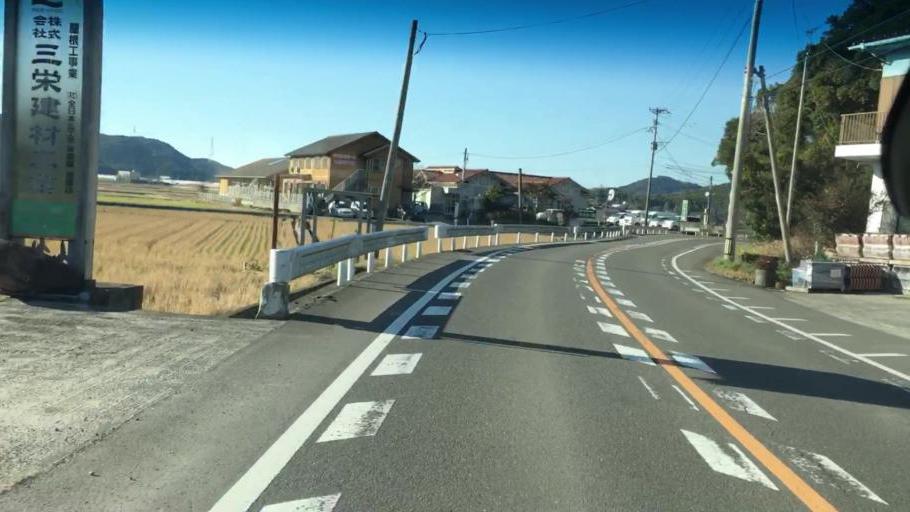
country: JP
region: Kagoshima
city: Satsumasendai
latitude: 31.8267
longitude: 130.2479
